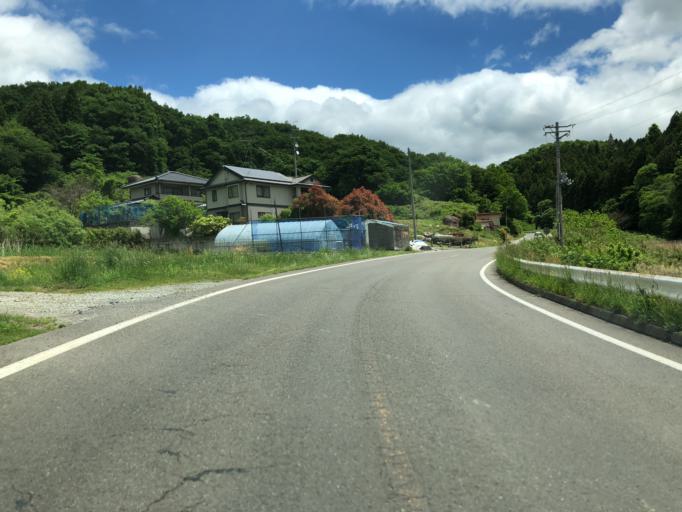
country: JP
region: Fukushima
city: Motomiya
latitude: 37.5191
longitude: 140.4515
